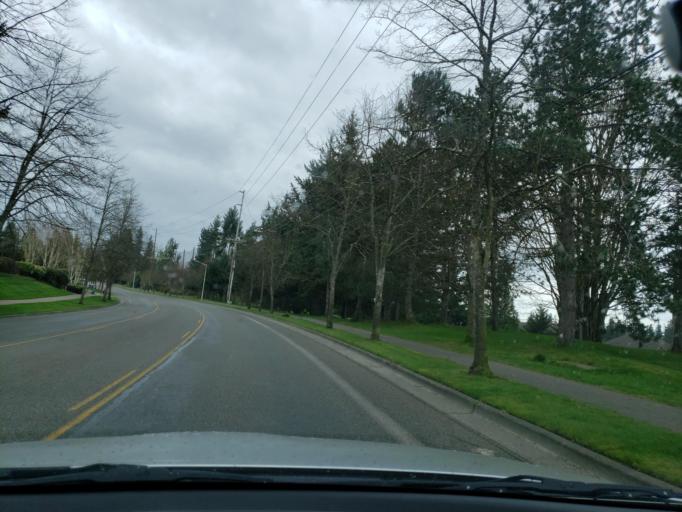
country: US
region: Washington
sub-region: Snohomish County
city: Meadowdale
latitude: 47.8921
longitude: -122.3123
